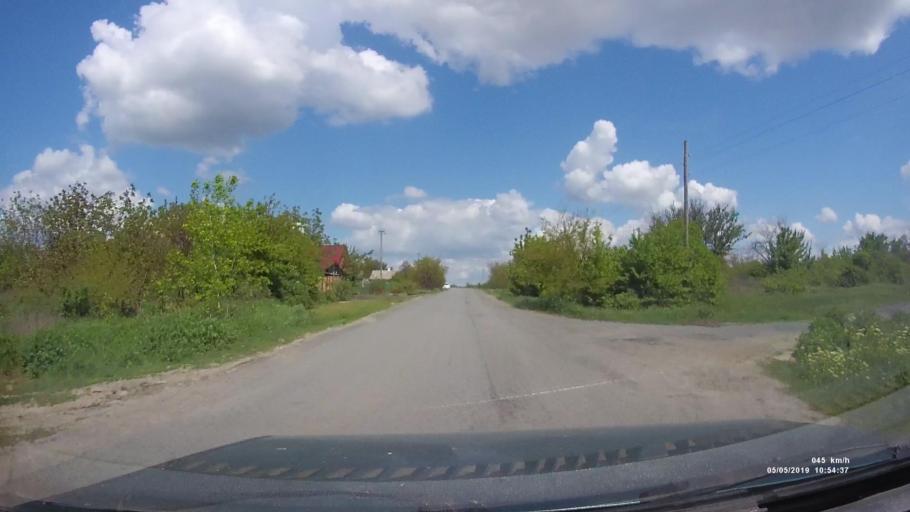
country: RU
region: Rostov
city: Ust'-Donetskiy
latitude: 47.6595
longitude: 40.8227
